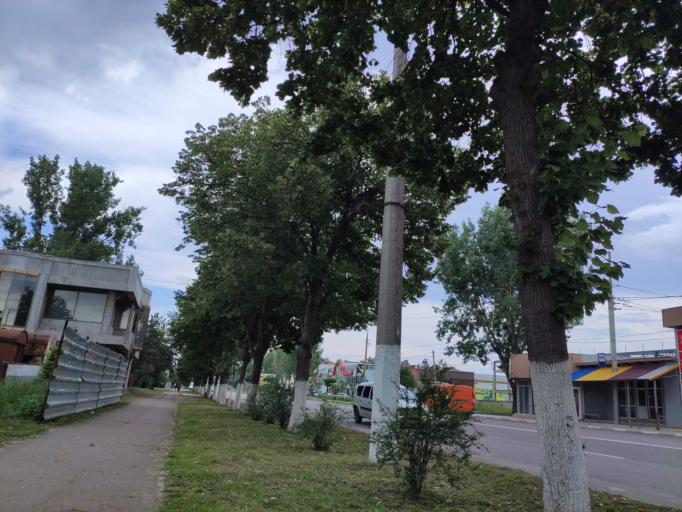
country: MD
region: Balti
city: Balti
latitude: 47.7615
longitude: 27.9409
